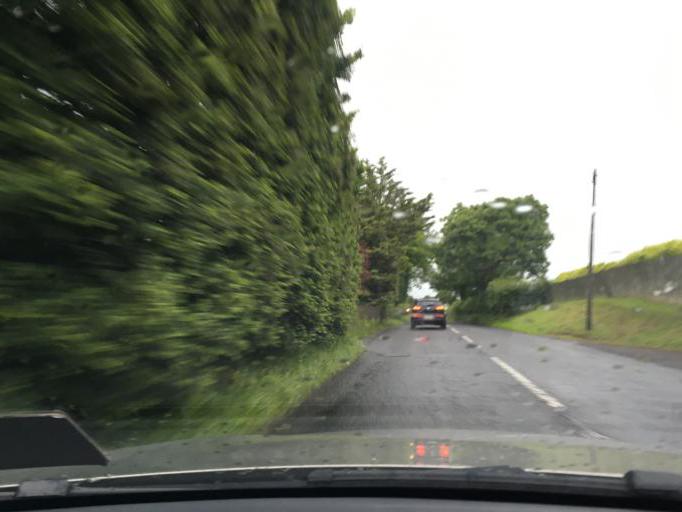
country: GB
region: Northern Ireland
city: Irvinestown
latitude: 54.4730
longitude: -7.7042
